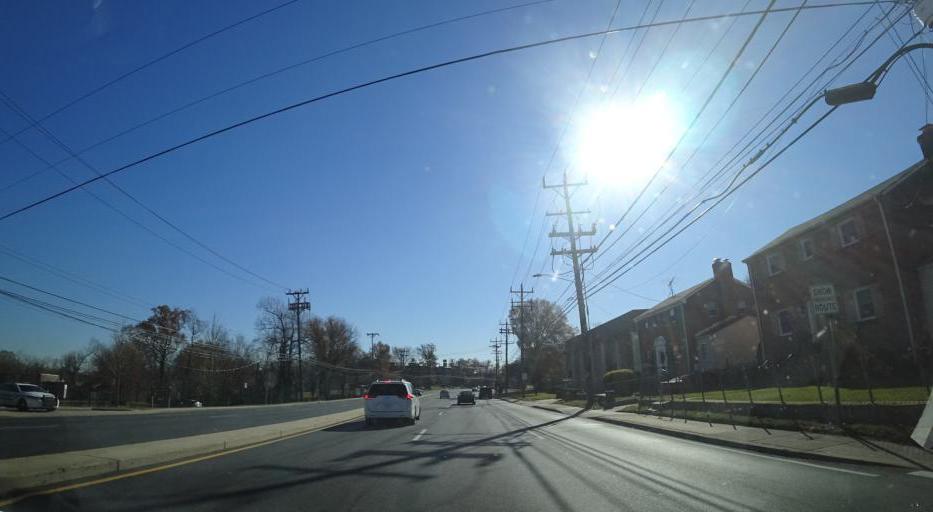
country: US
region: Maryland
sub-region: Prince George's County
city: Langley Park
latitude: 38.9987
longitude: -76.9949
